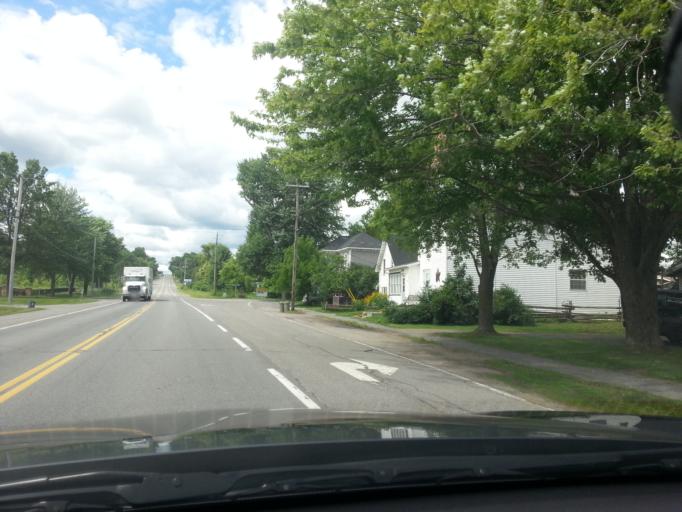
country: CA
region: Ontario
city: Perth
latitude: 44.6996
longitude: -76.1866
